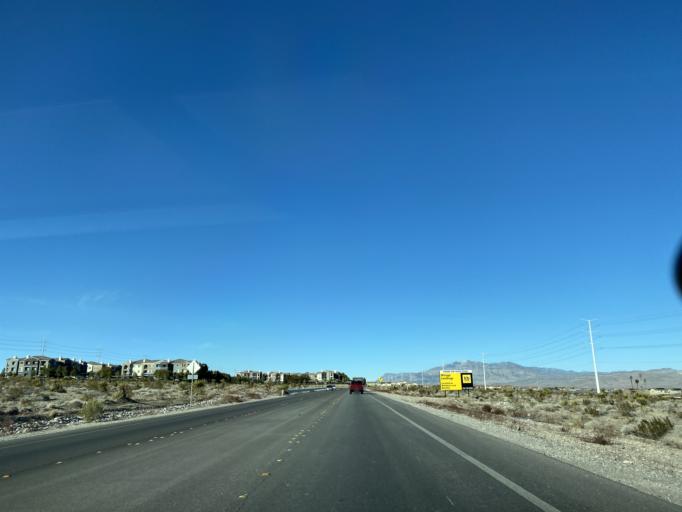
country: US
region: Nevada
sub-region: Clark County
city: Summerlin South
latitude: 36.2710
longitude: -115.3300
